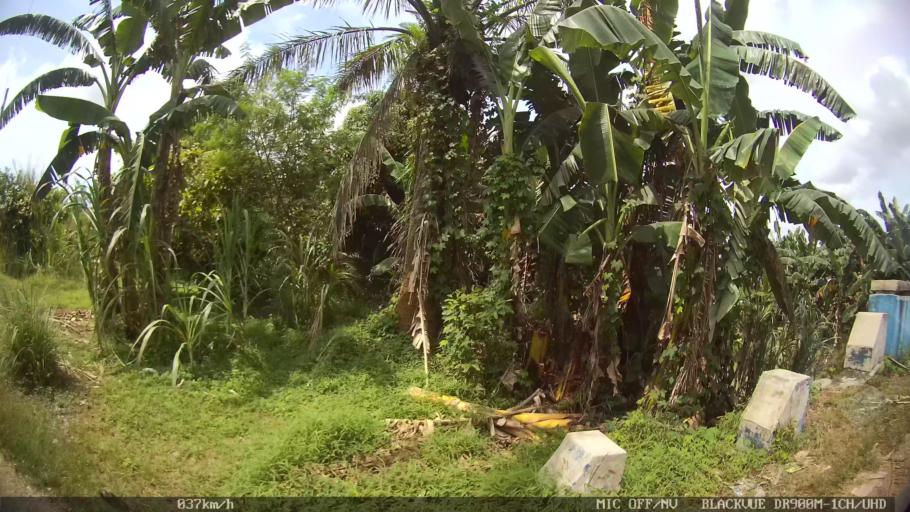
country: ID
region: North Sumatra
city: Percut
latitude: 3.5682
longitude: 98.8530
